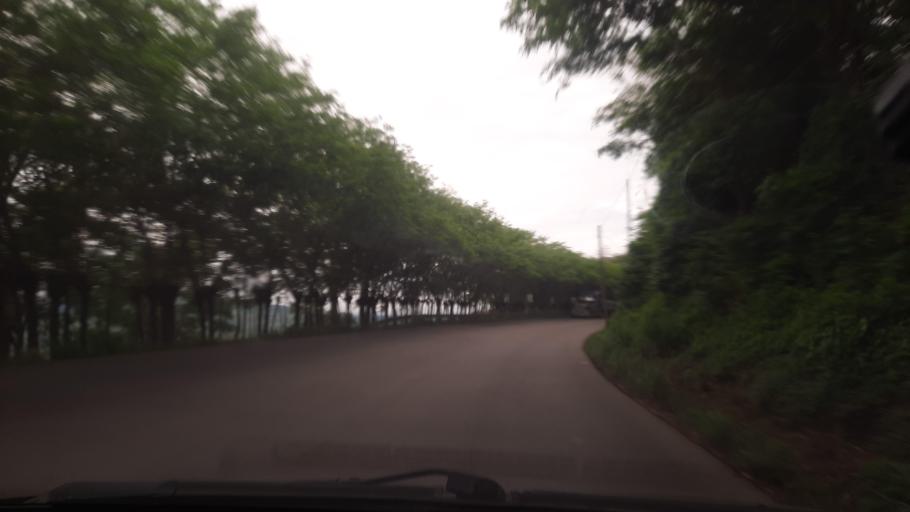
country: GT
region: Izabal
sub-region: Municipio de Los Amates
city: Los Amates
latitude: 15.2517
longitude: -89.1222
